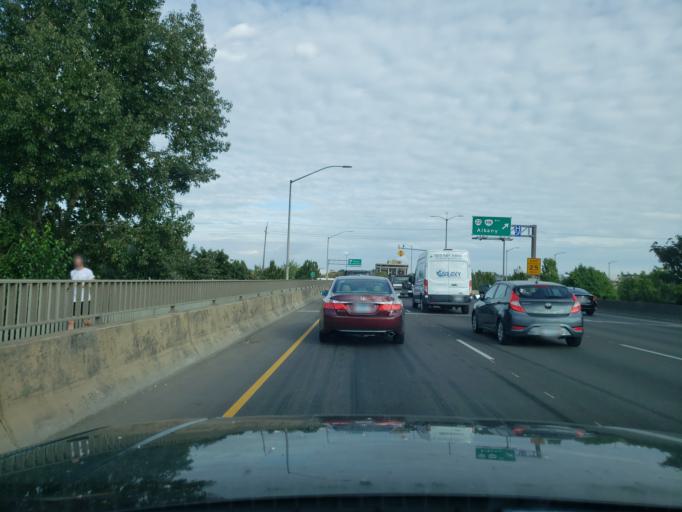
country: US
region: Oregon
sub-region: Marion County
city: Salem
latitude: 44.9447
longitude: -123.0424
